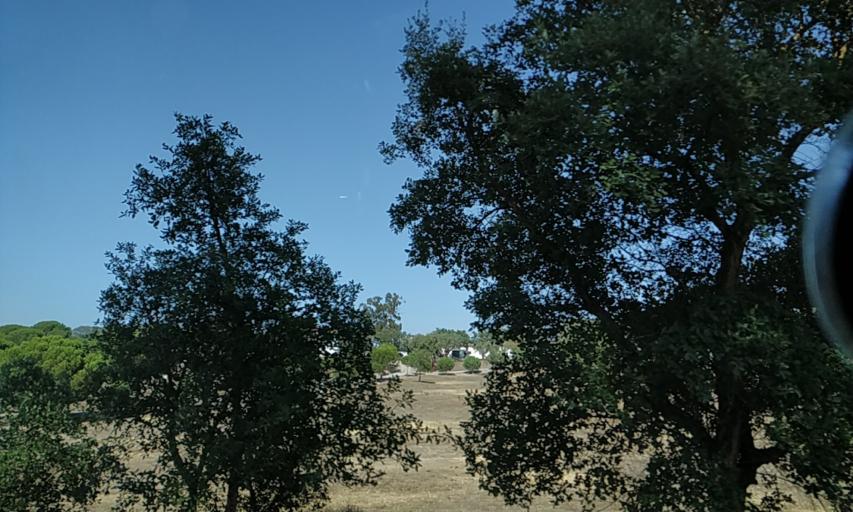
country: PT
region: Santarem
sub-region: Coruche
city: Coruche
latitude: 38.8535
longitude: -8.5449
